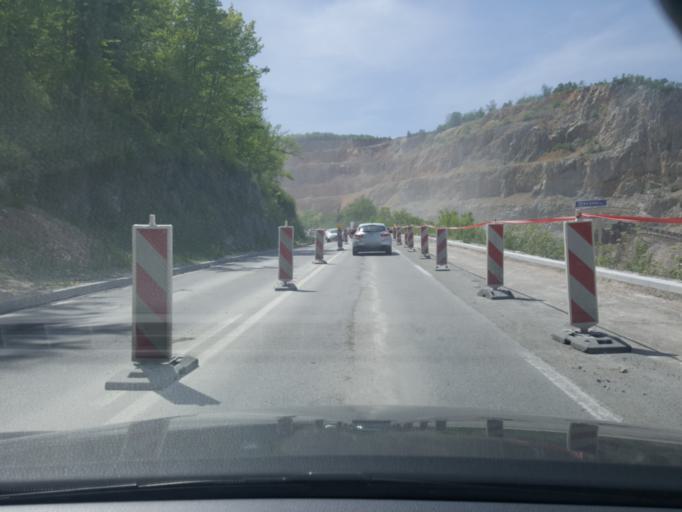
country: RS
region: Central Serbia
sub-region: Zlatiborski Okrug
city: Uzice
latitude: 43.8434
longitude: 19.8129
